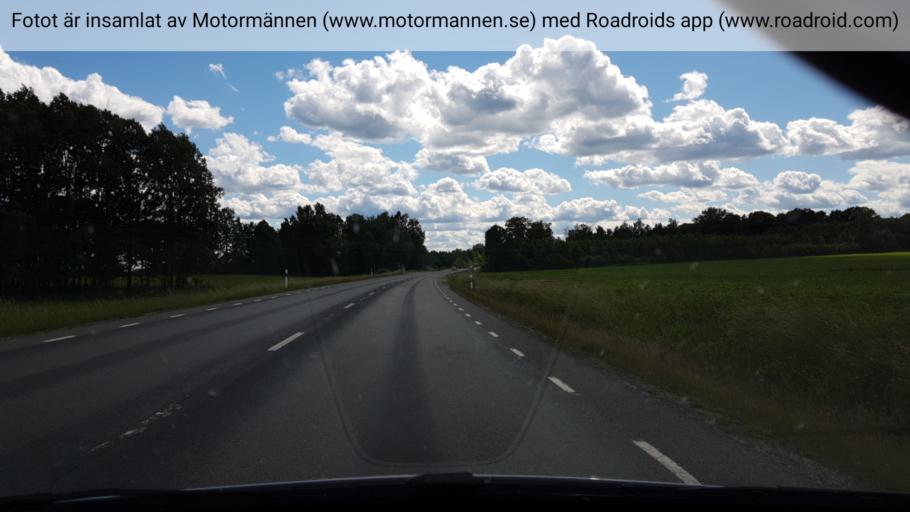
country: SE
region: Vaestra Goetaland
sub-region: Hjo Kommun
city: Hjo
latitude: 58.2669
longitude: 14.2592
